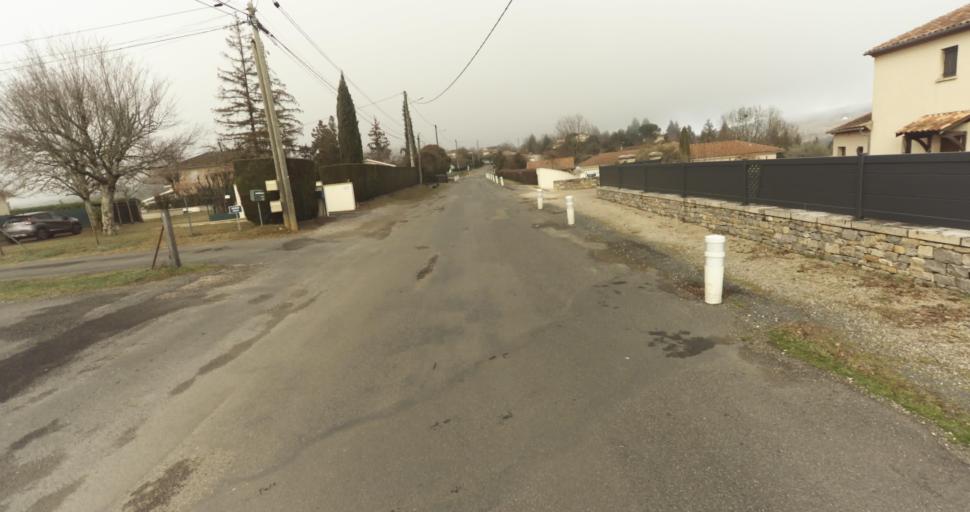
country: FR
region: Midi-Pyrenees
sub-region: Departement du Lot
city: Figeac
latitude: 44.6213
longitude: 2.0234
